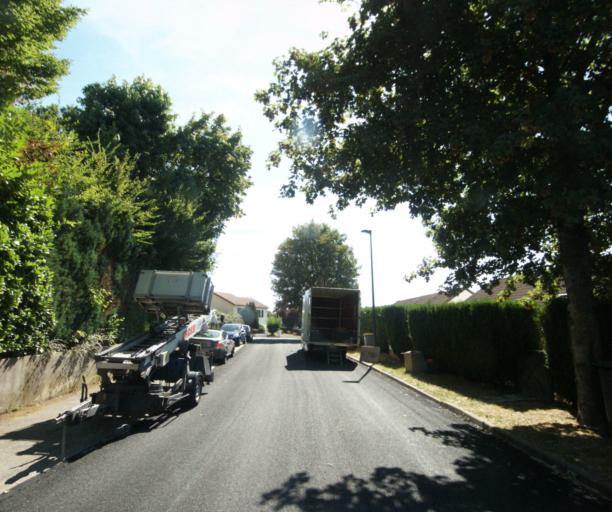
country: FR
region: Lorraine
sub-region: Departement des Vosges
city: Chantraine
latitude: 48.1833
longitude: 6.4323
